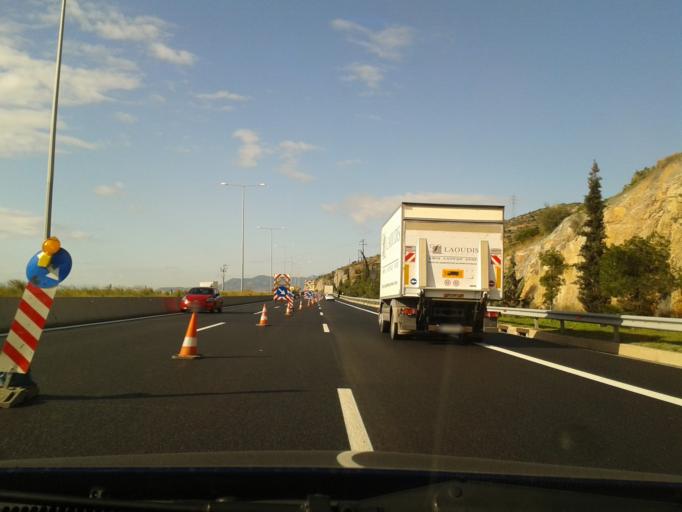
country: GR
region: Attica
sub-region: Nomarchia Dytikis Attikis
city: Vlychada
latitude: 38.0291
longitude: 23.4627
